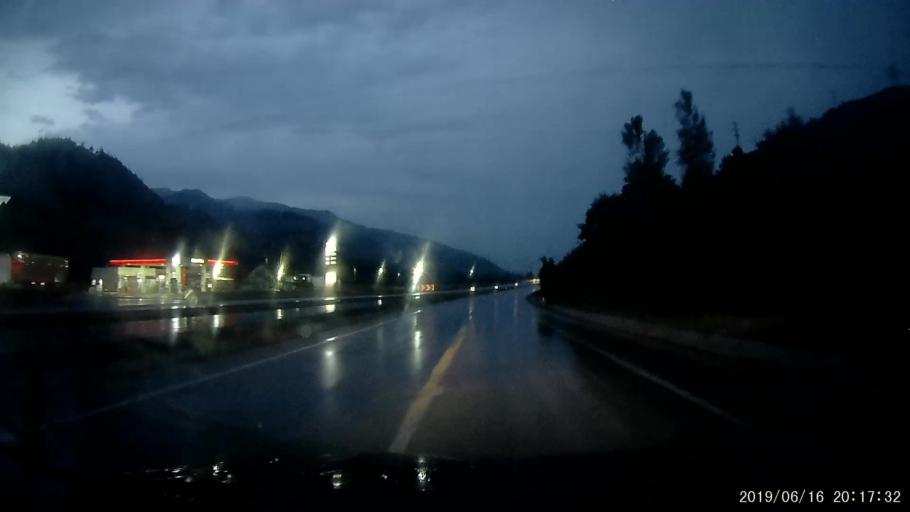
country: TR
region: Tokat
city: Resadiye
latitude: 40.3655
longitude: 37.4207
